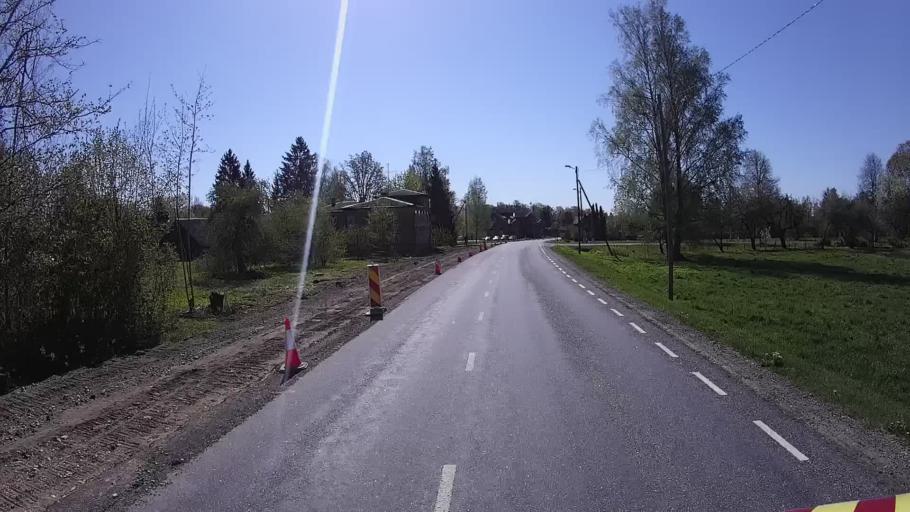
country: EE
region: Paernumaa
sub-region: Tootsi vald
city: Tootsi
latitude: 58.4873
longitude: 24.8123
